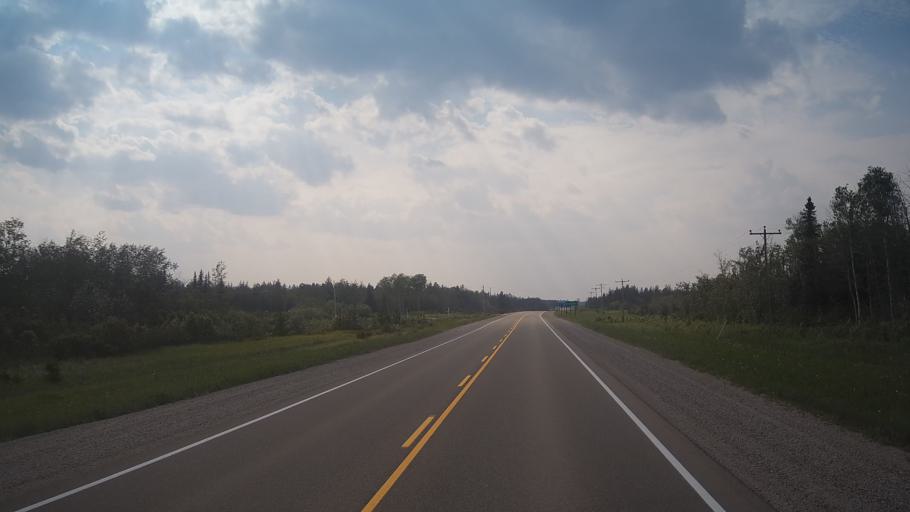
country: CA
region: Ontario
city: Kapuskasing
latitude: 49.5073
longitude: -82.7588
